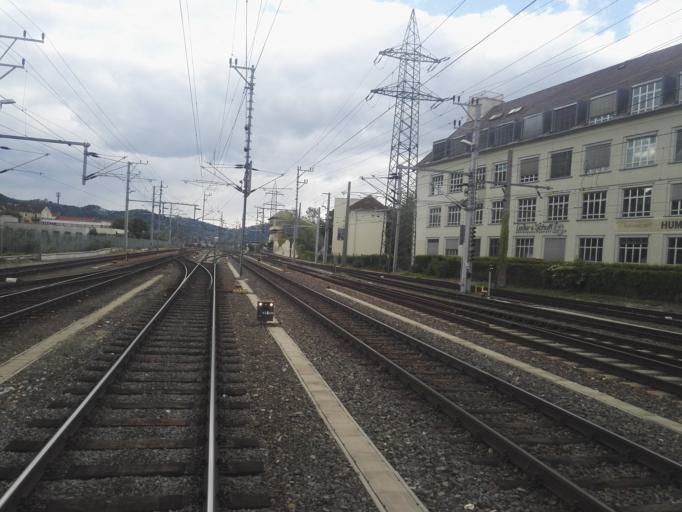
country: AT
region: Styria
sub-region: Graz Stadt
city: Goesting
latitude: 47.0816
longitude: 15.4127
